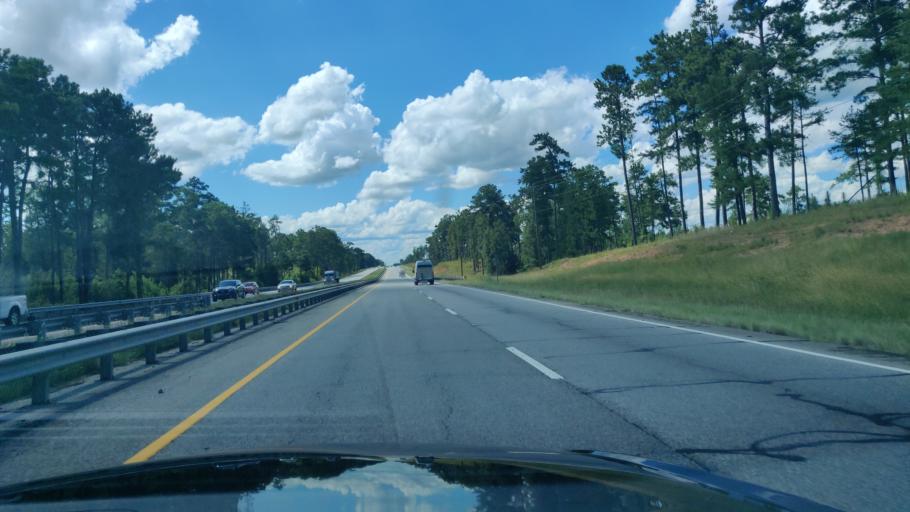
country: US
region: Georgia
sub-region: Chattahoochee County
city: Cusseta
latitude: 32.3496
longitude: -84.8325
